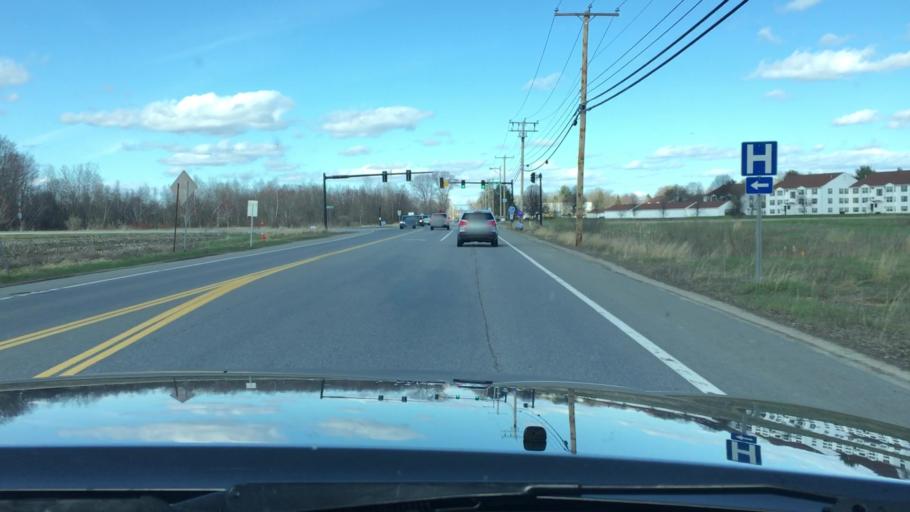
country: US
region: New Hampshire
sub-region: Merrimack County
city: Concord
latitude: 43.1872
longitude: -71.5562
